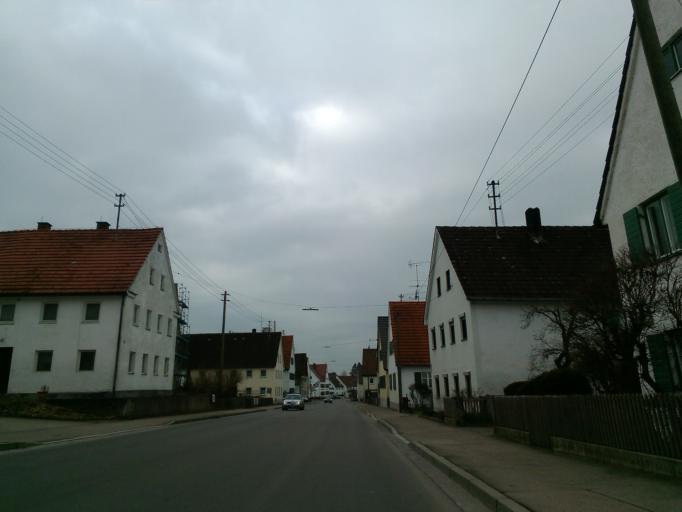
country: DE
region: Bavaria
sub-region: Swabia
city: Ustersbach
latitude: 48.3169
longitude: 10.6441
